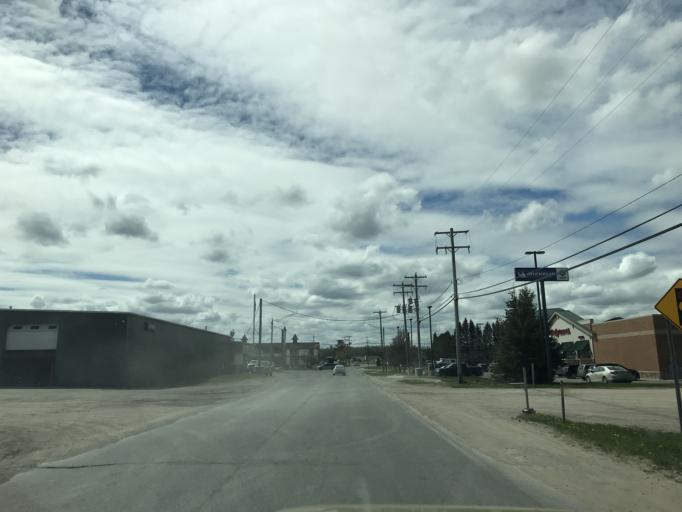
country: US
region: Michigan
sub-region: Otsego County
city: Gaylord
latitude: 45.0287
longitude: -84.6942
